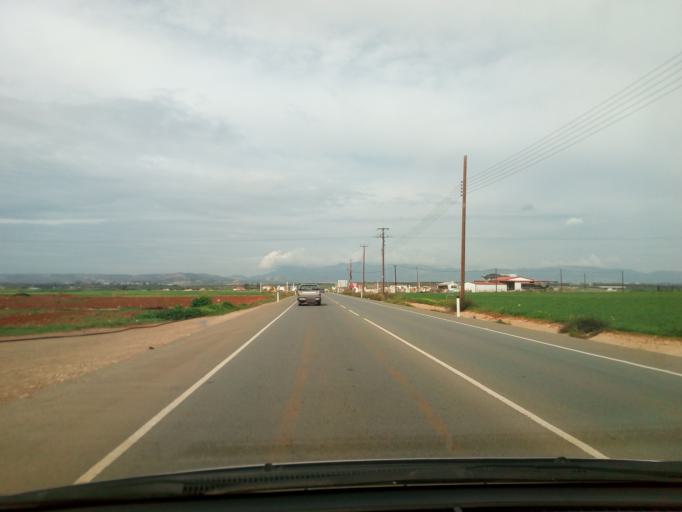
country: CY
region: Lefkosia
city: Akaki
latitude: 35.1448
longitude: 33.1559
